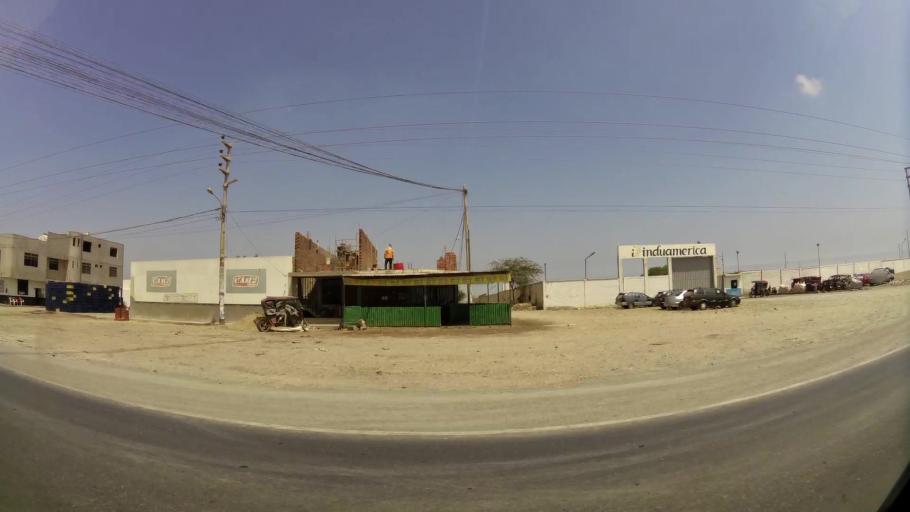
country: PE
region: La Libertad
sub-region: Provincia de Pacasmayo
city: Pacasmayo
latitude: -7.4170
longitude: -79.5473
